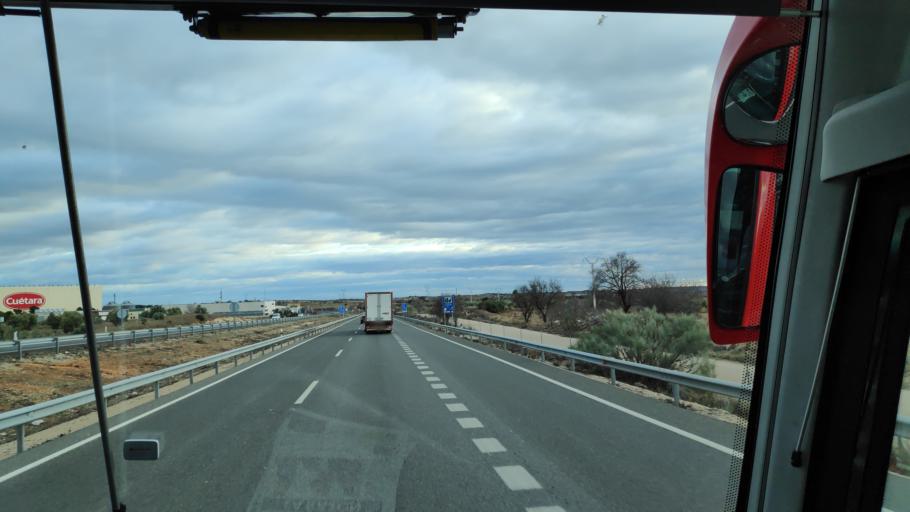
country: ES
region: Madrid
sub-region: Provincia de Madrid
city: Villarejo de Salvanes
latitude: 40.1803
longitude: -3.2968
